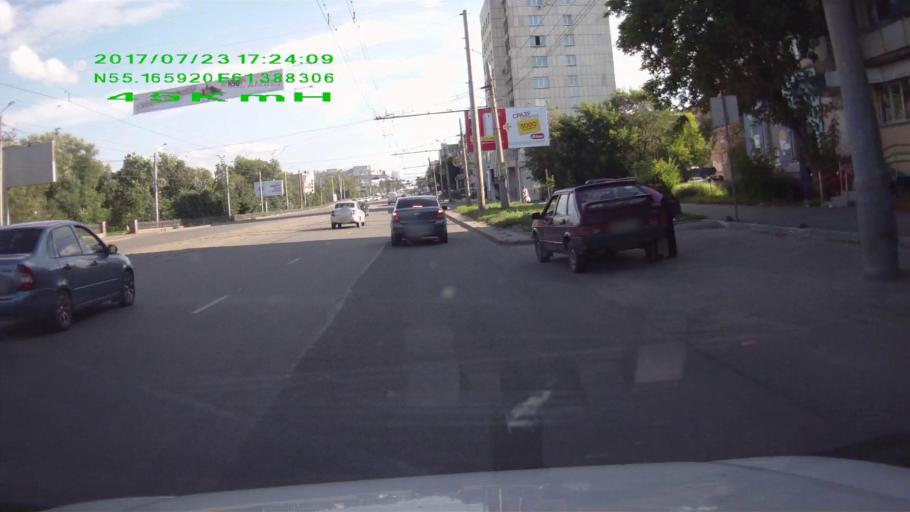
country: RU
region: Chelyabinsk
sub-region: Gorod Chelyabinsk
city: Chelyabinsk
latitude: 55.1656
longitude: 61.3883
